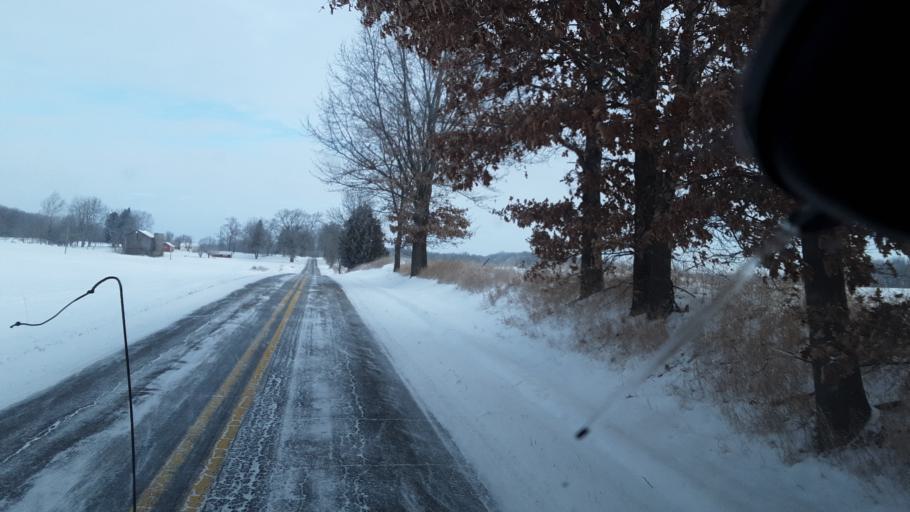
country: US
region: Michigan
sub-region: Ingham County
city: Leslie
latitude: 42.3516
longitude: -84.4826
